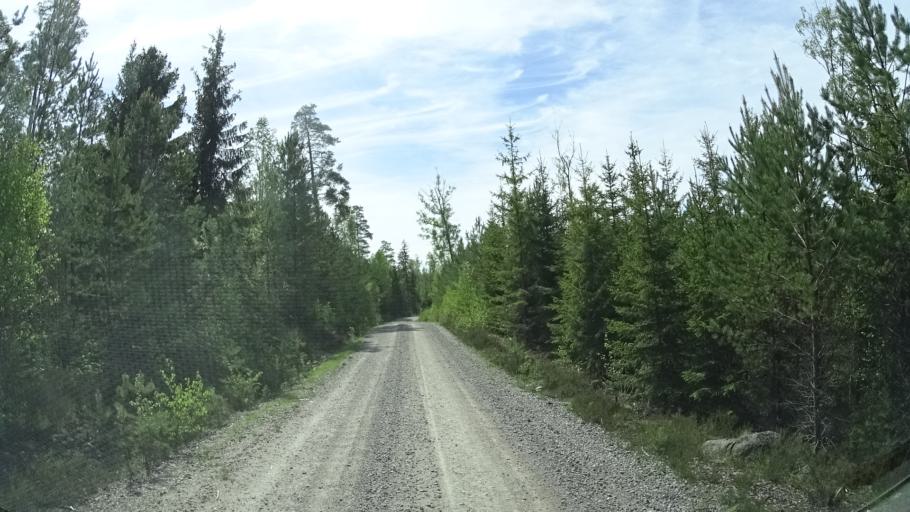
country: SE
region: OEstergoetland
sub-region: Finspangs Kommun
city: Finspang
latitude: 58.7810
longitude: 15.8469
